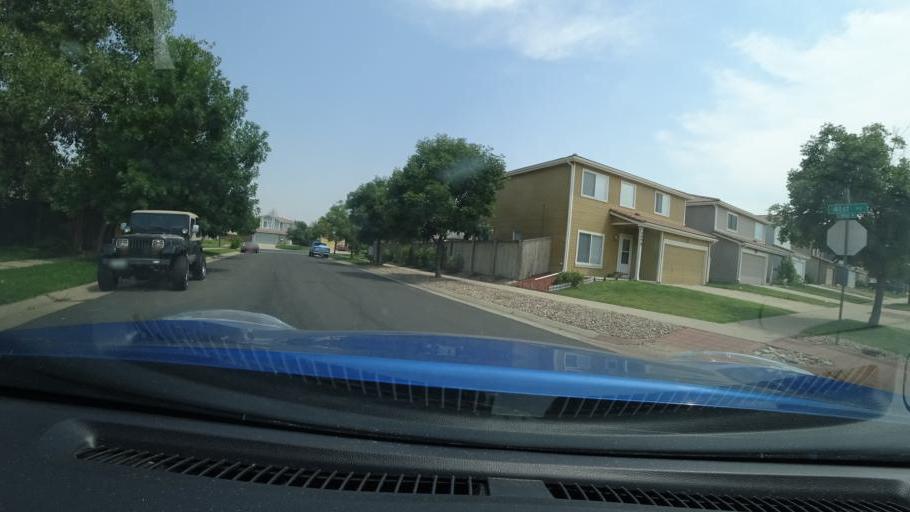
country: US
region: Colorado
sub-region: Adams County
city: Aurora
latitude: 39.7729
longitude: -104.7399
